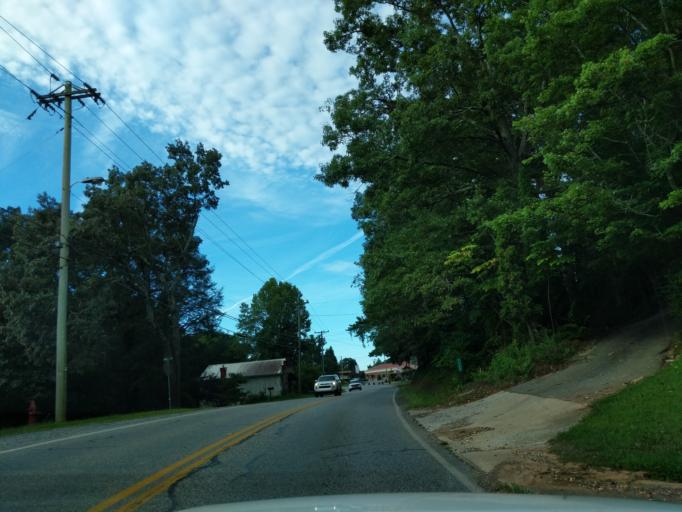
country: US
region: Georgia
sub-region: Fannin County
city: McCaysville
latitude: 34.9740
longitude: -84.3709
